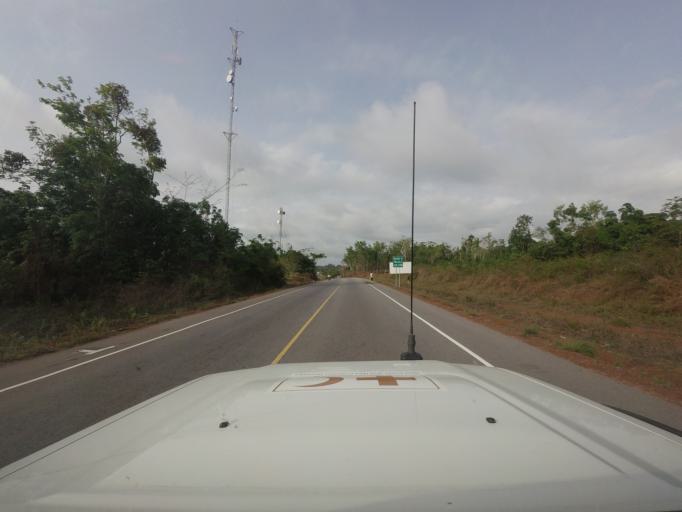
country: LR
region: Bong
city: Gbarnga
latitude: 7.0066
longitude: -9.2847
